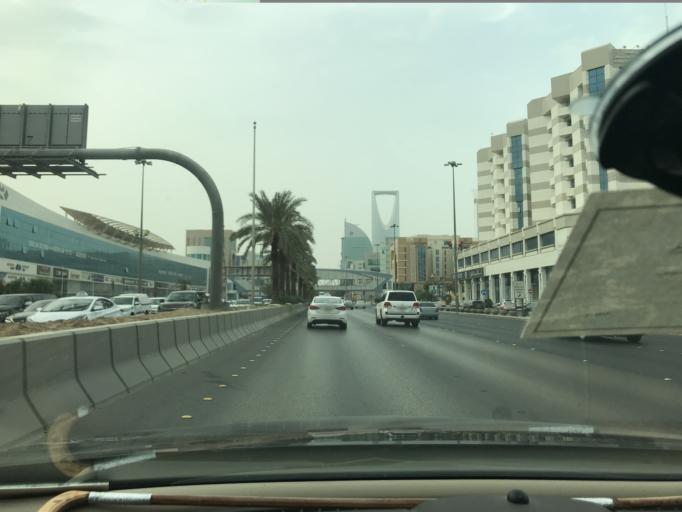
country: SA
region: Ar Riyad
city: Riyadh
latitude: 24.6979
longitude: 46.6792
